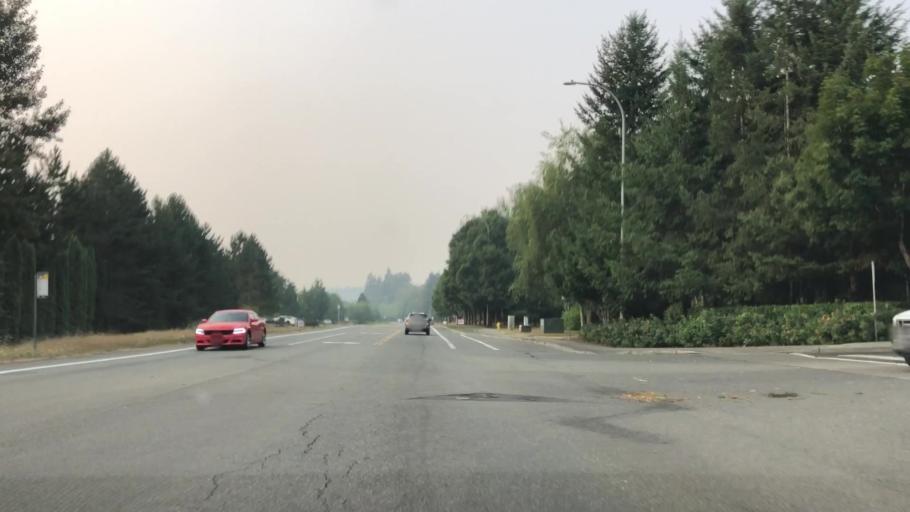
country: US
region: Washington
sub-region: King County
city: Redmond
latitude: 47.6955
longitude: -122.1516
